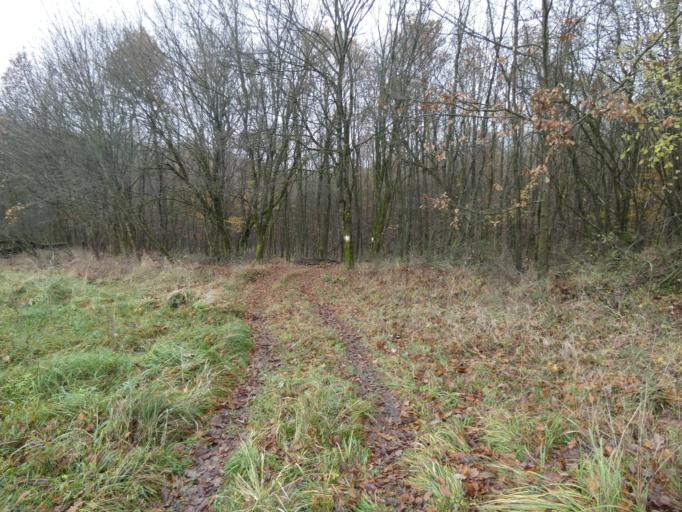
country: HU
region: Pest
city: Kismaros
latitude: 47.8929
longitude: 18.9843
